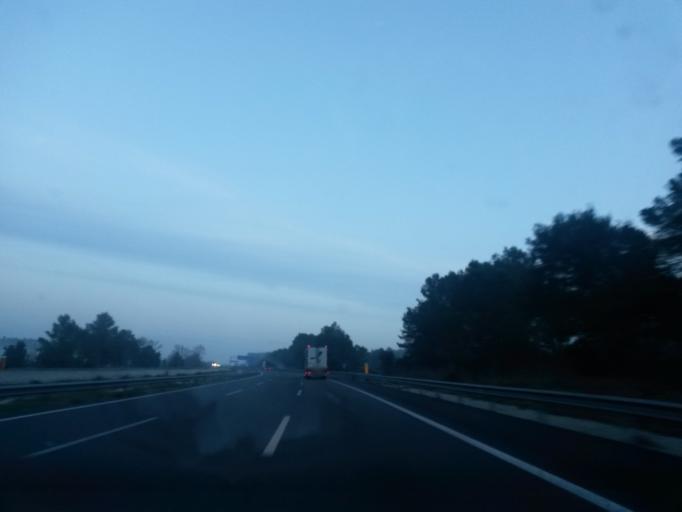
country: ES
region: Catalonia
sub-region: Provincia de Girona
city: Vilademuls
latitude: 42.1132
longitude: 2.9133
